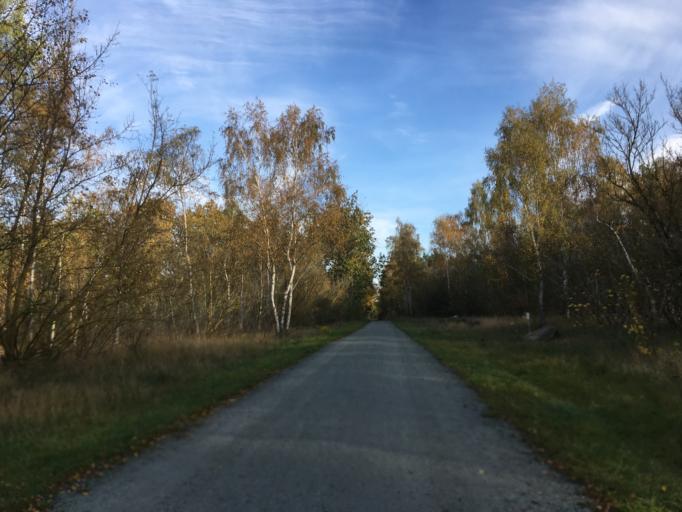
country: DE
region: Berlin
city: Buch
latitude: 52.6592
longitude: 13.4835
